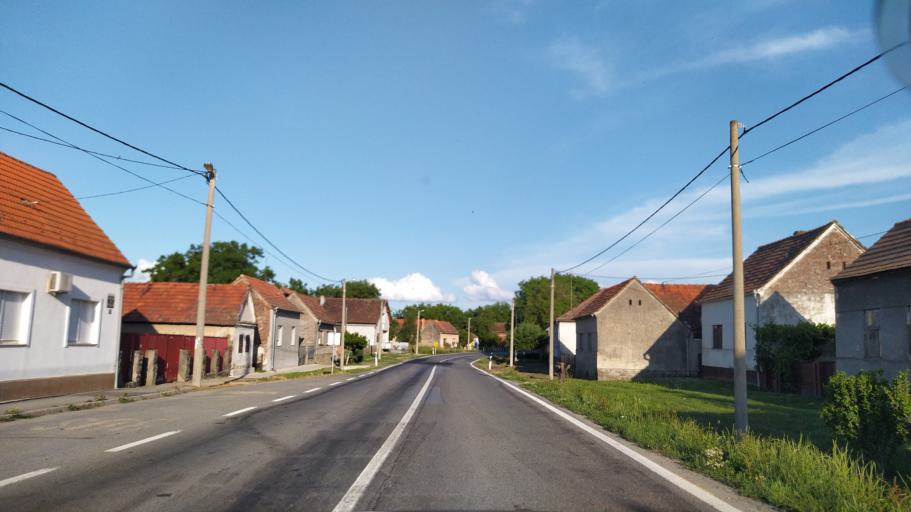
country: HR
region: Virovitick-Podravska
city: Slatina
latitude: 45.6819
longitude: 17.7424
